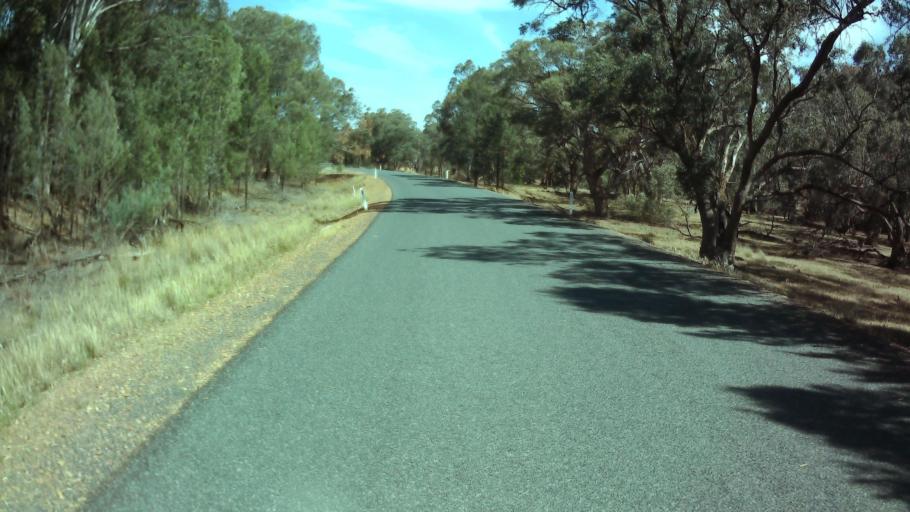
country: AU
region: New South Wales
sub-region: Weddin
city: Grenfell
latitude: -34.0784
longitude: 148.1456
